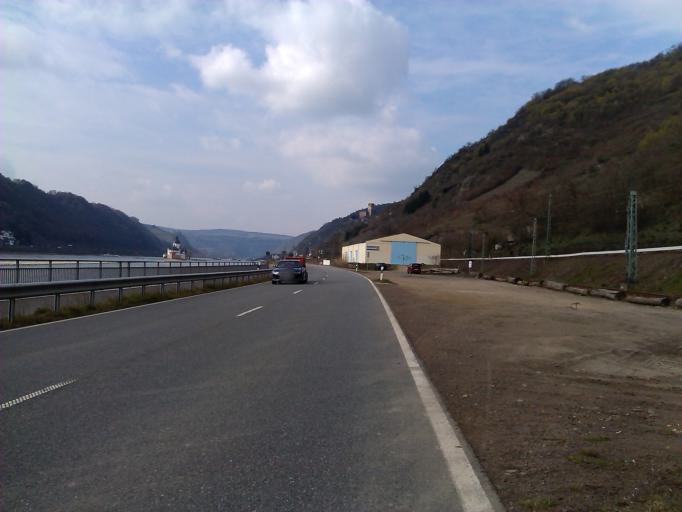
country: DE
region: Rheinland-Pfalz
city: Kaub
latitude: 50.0771
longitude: 7.7767
